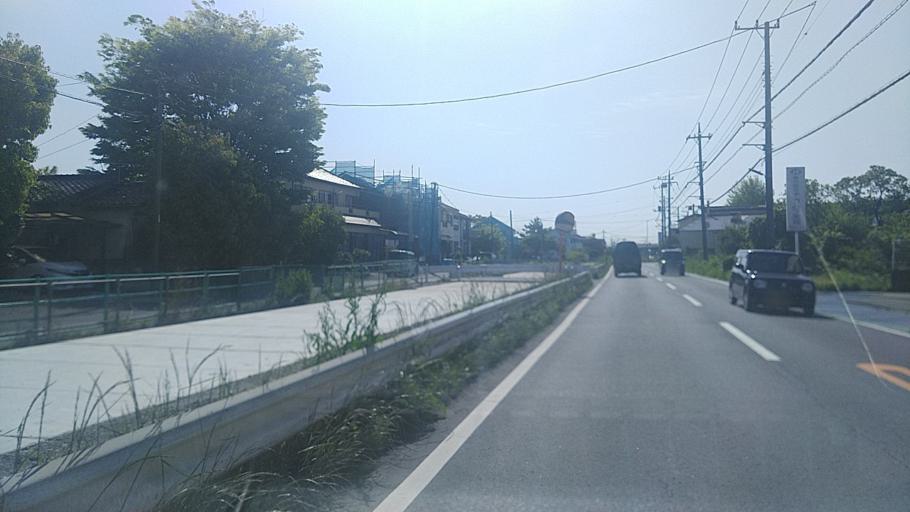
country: JP
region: Saitama
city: Koshigaya
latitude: 35.8734
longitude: 139.7640
